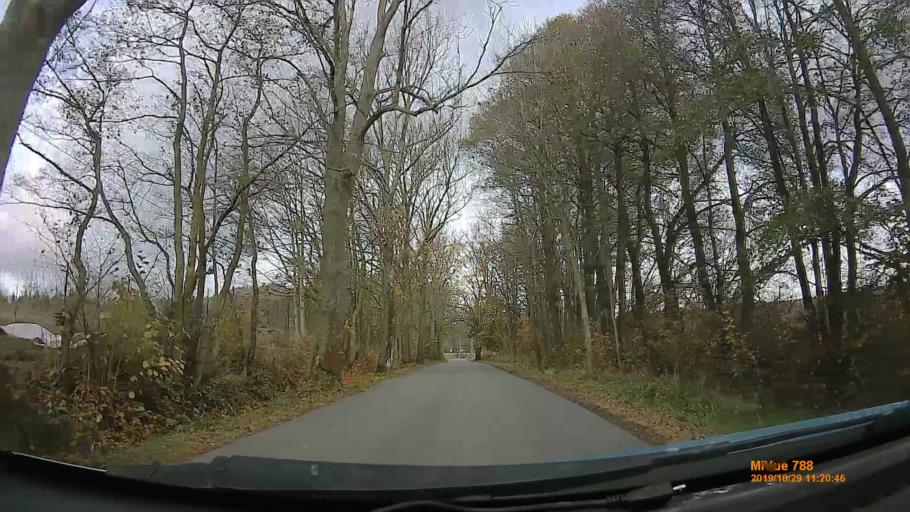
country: PL
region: Lower Silesian Voivodeship
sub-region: Powiat klodzki
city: Szczytna
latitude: 50.4241
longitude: 16.4385
